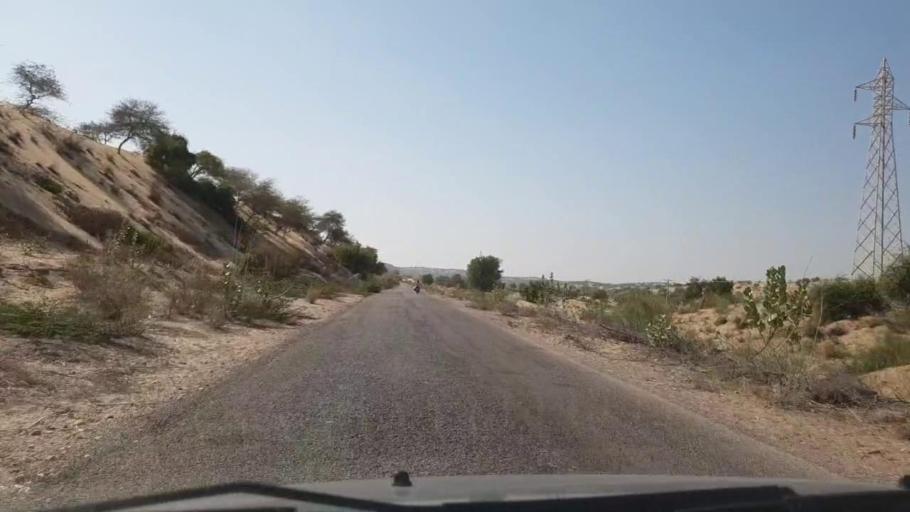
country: PK
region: Sindh
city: Diplo
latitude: 24.5746
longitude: 69.6885
